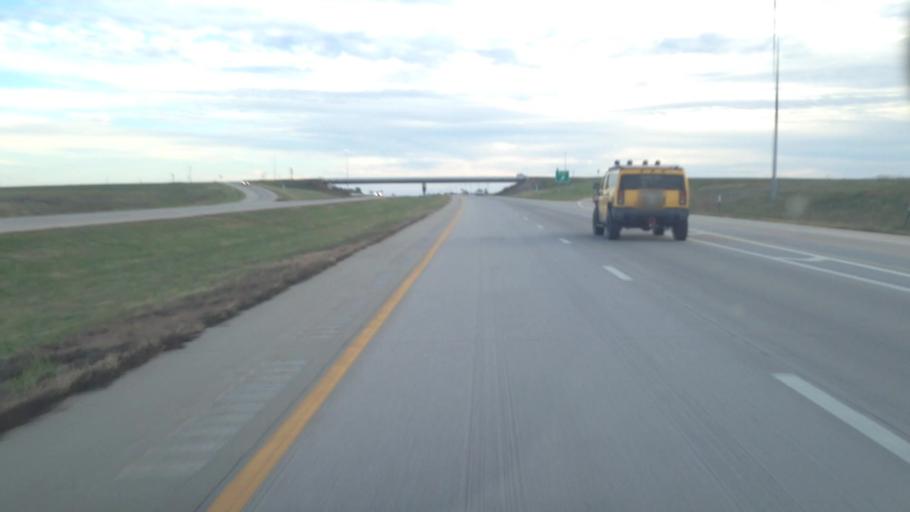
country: US
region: Kansas
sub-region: Douglas County
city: Baldwin City
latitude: 38.8369
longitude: -95.2689
